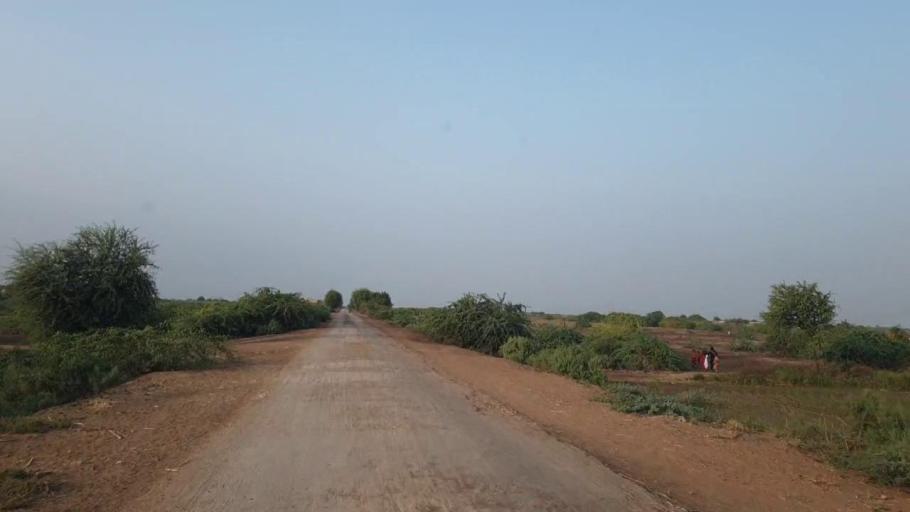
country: PK
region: Sindh
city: Tando Ghulam Ali
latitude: 25.0710
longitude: 68.9595
